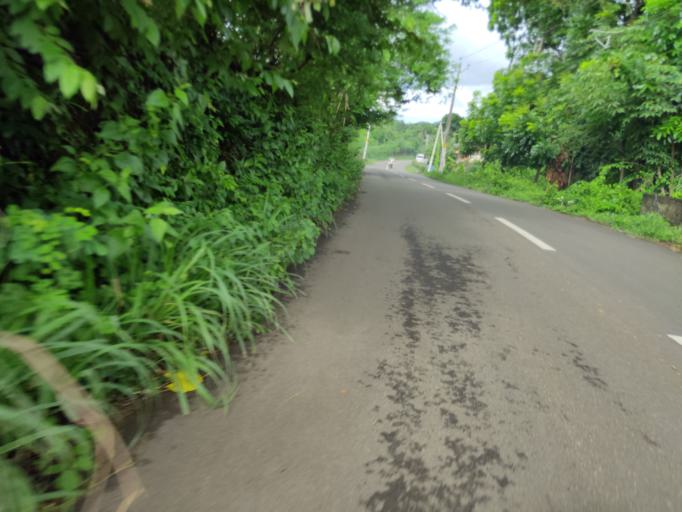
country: IN
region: Kerala
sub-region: Malappuram
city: Manjeri
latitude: 11.1446
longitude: 76.1418
